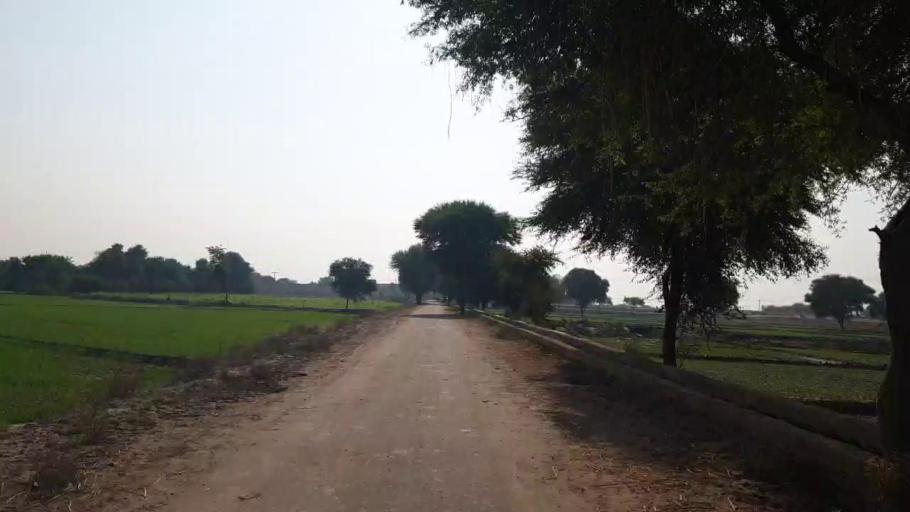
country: PK
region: Sindh
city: Sehwan
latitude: 26.4393
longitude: 67.8406
